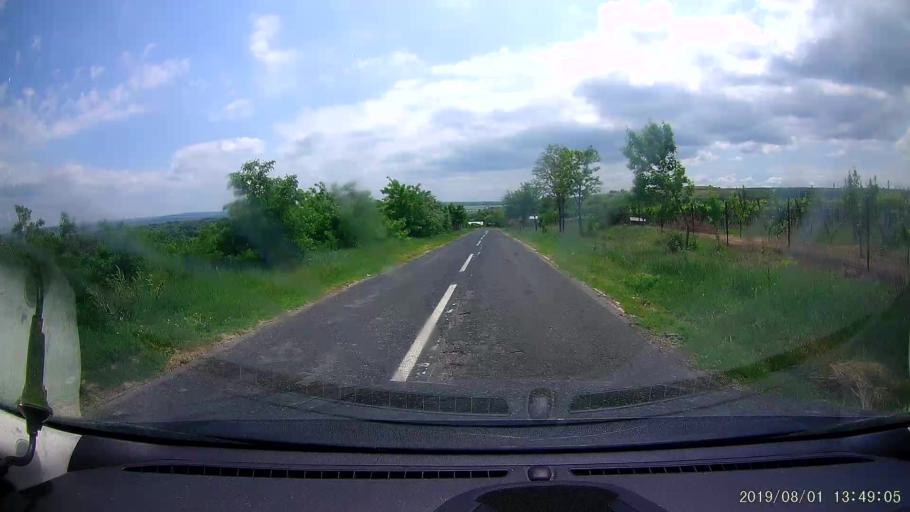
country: RO
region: Galati
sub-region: Comuna Oancea
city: Oancea
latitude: 45.8994
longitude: 28.1092
